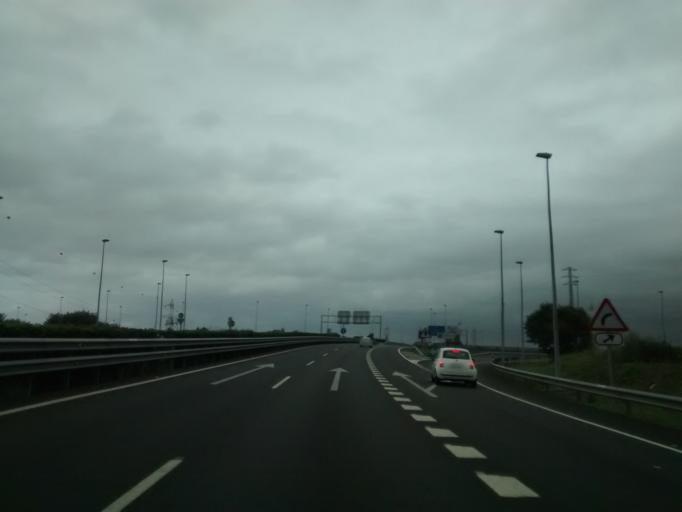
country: ES
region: Cantabria
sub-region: Provincia de Cantabria
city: Camargo
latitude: 43.4376
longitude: -3.8643
